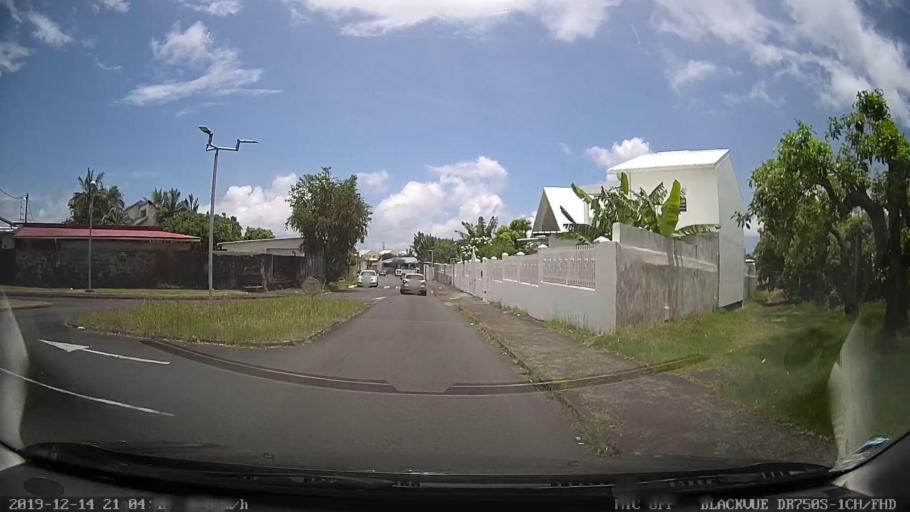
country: RE
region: Reunion
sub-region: Reunion
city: Saint-Andre
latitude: -20.9565
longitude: 55.6550
